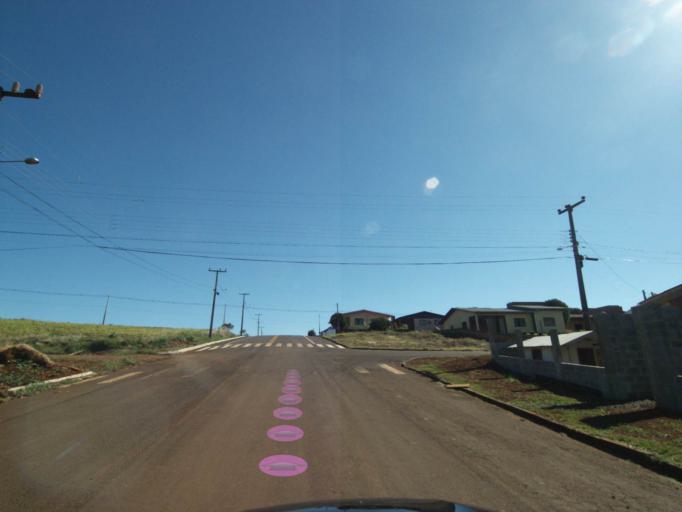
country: BR
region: Parana
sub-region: Coronel Vivida
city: Coronel Vivida
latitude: -26.1462
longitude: -52.3822
